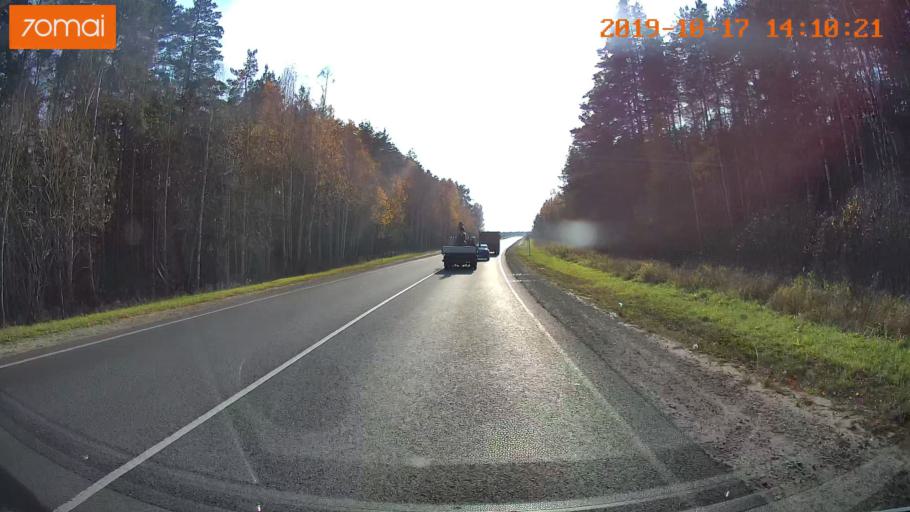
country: RU
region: Rjazan
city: Spas-Klepiki
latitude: 55.0798
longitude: 40.0513
